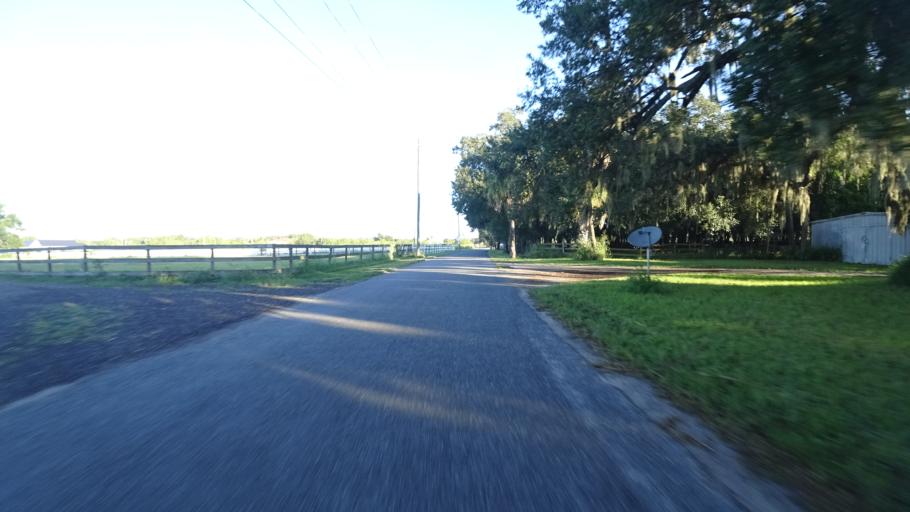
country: US
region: Florida
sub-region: Manatee County
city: Ellenton
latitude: 27.5360
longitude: -82.5401
